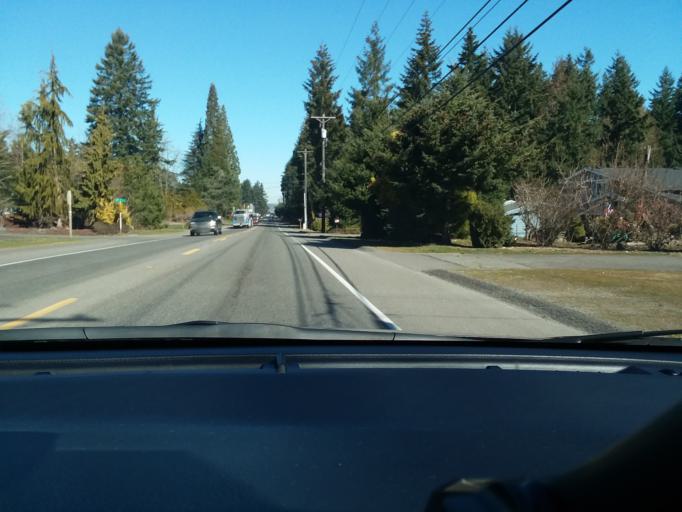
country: US
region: Washington
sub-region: Pierce County
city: Waller
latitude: 47.1874
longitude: -122.3573
